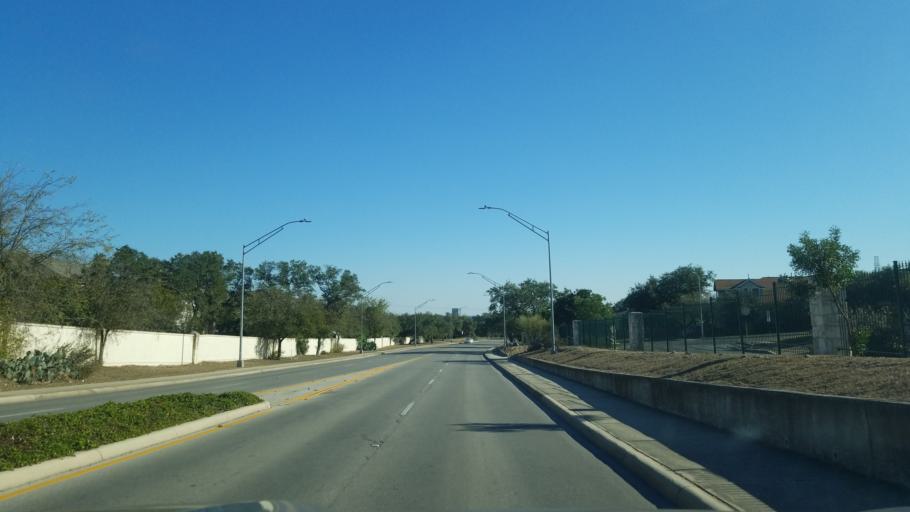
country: US
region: Texas
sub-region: Bexar County
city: Hollywood Park
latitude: 29.6353
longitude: -98.4838
